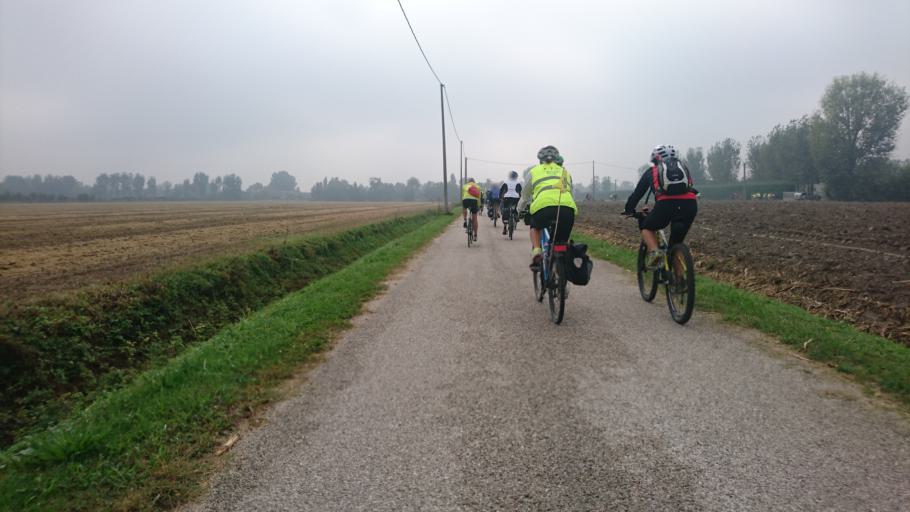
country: IT
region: Veneto
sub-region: Provincia di Padova
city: Stanghella
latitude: 45.1527
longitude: 11.7834
